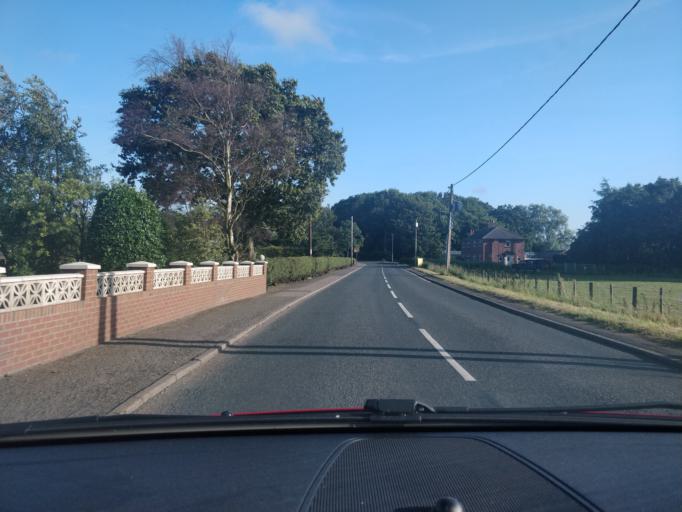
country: GB
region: England
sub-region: Lancashire
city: Banks
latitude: 53.6595
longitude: -2.8789
